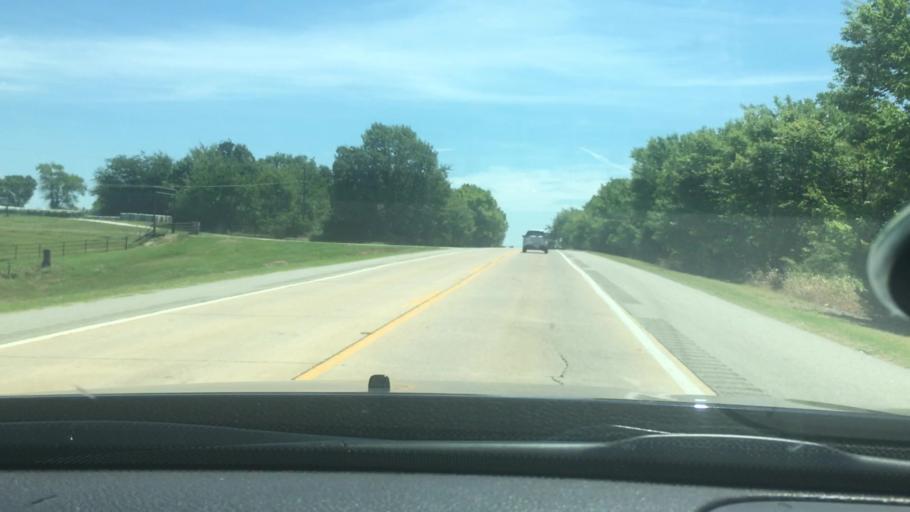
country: US
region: Oklahoma
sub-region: Bryan County
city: Durant
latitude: 34.0118
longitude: -96.1174
